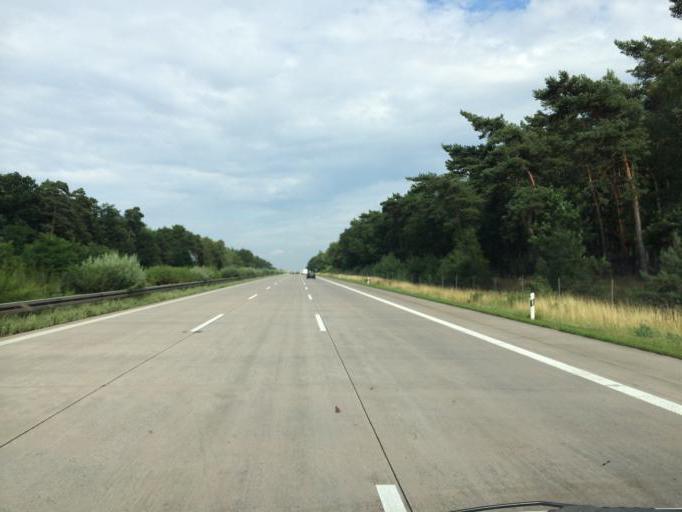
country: DE
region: Saxony-Anhalt
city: Schermen
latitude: 52.2282
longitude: 11.8555
